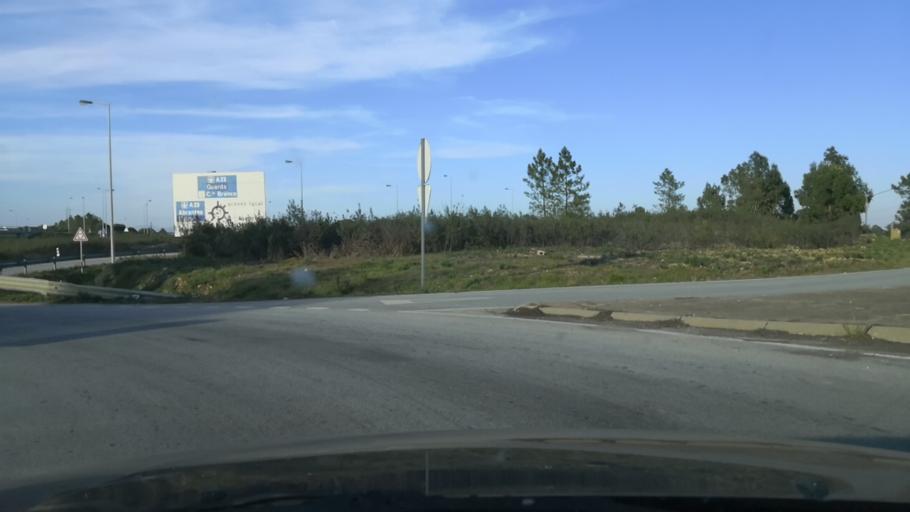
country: PT
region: Castelo Branco
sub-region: Castelo Branco
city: Castelo Branco
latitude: 39.7845
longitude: -7.5695
